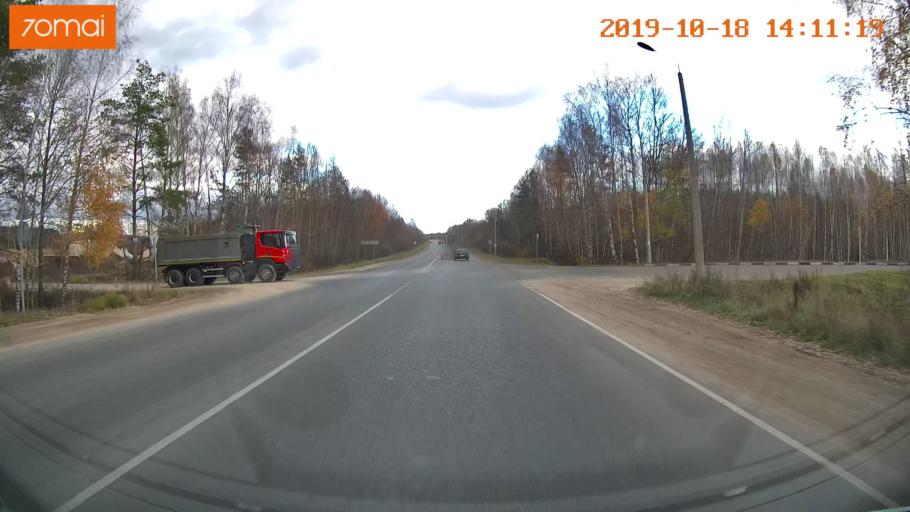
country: RU
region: Rjazan
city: Spas-Klepiki
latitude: 55.1393
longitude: 40.2218
